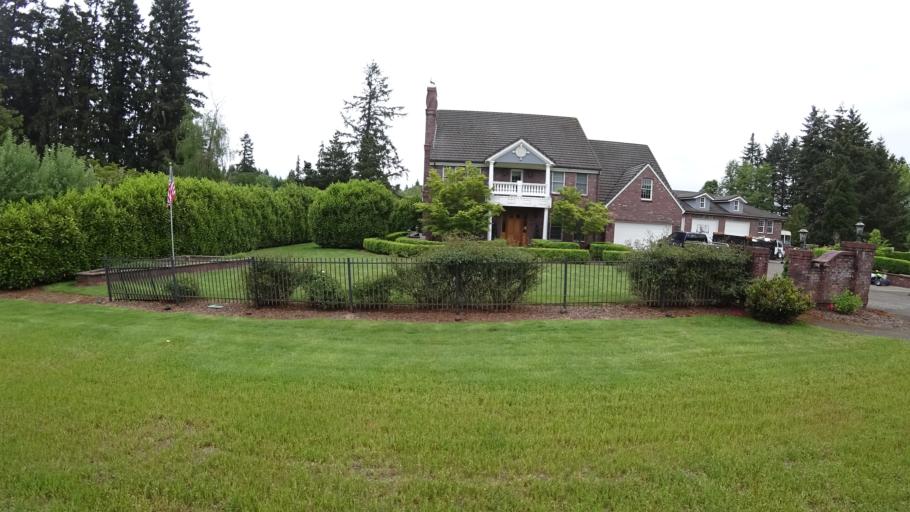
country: US
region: Oregon
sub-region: Washington County
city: Aloha
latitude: 45.4842
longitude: -122.9123
